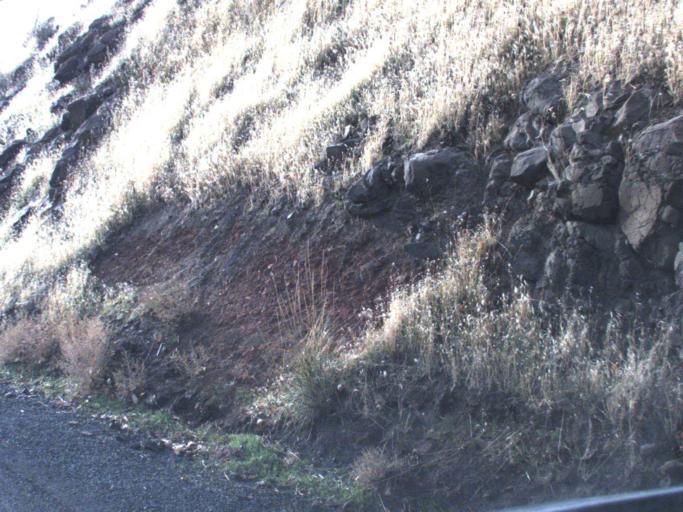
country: US
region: Washington
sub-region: Garfield County
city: Pomeroy
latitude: 46.4656
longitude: -117.6766
